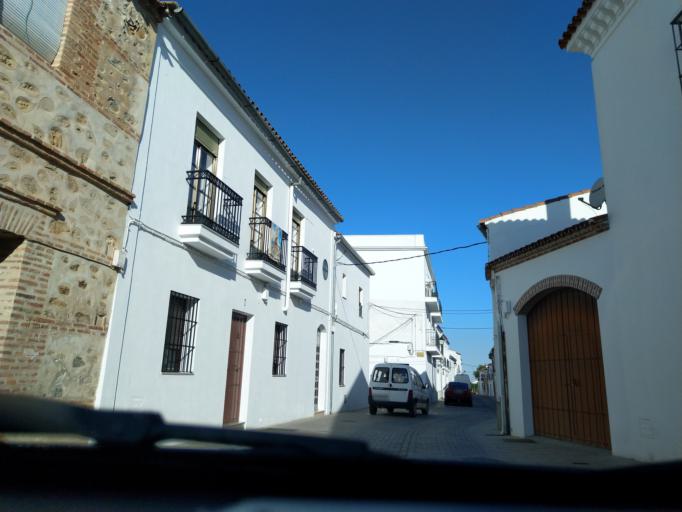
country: ES
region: Extremadura
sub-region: Provincia de Badajoz
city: Llerena
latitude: 38.2396
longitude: -6.0158
